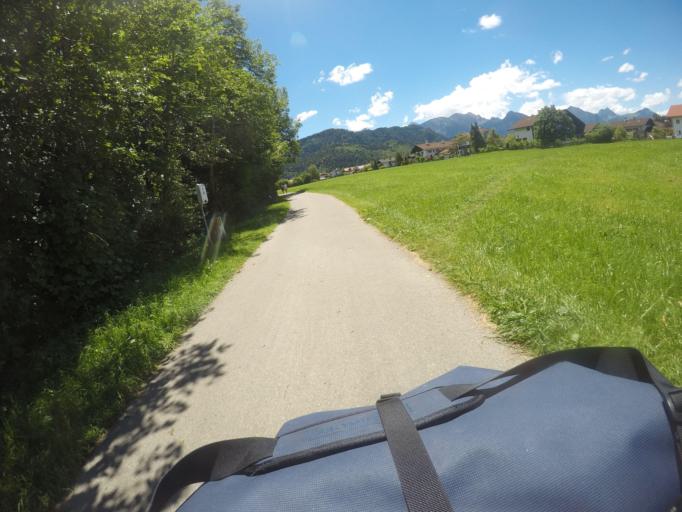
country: DE
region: Bavaria
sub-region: Swabia
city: Fuessen
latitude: 47.5747
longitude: 10.7120
